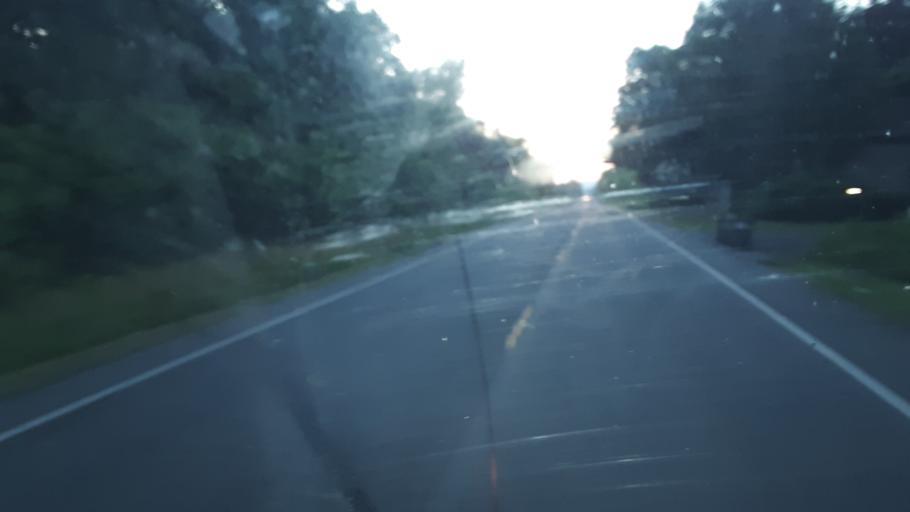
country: US
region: New York
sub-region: Saratoga County
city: Ballston Spa
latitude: 42.9952
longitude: -73.9170
